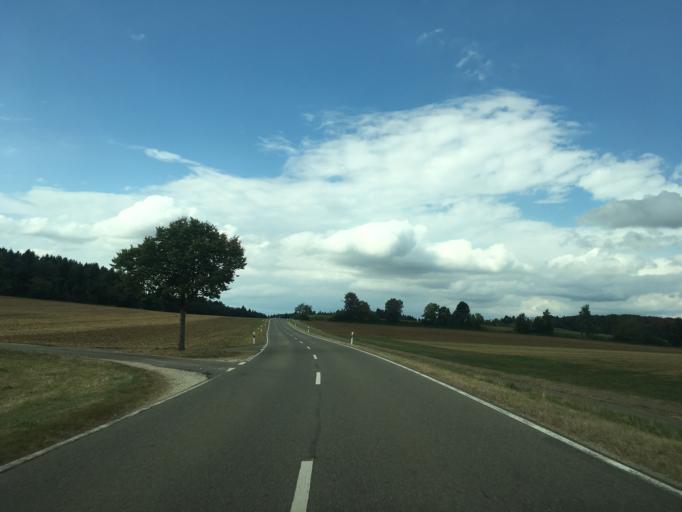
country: DE
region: Baden-Wuerttemberg
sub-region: Tuebingen Region
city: Gomadingen
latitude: 48.3508
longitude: 9.4099
